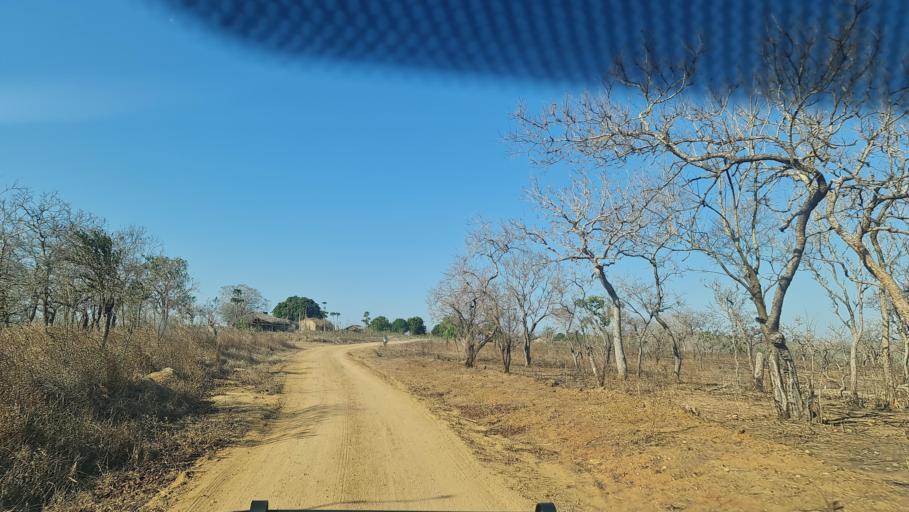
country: MZ
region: Nampula
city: Nacala
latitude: -13.9452
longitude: 40.4800
